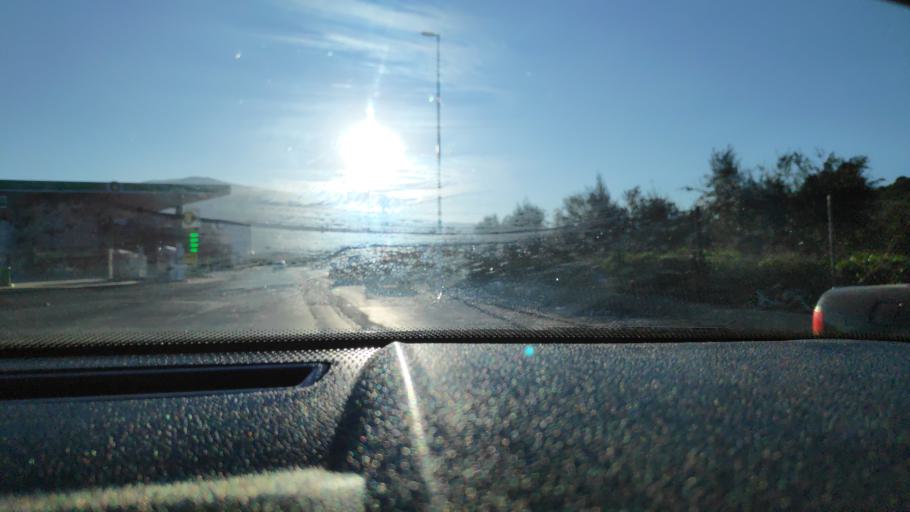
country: ES
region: Andalusia
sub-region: Provincia de Jaen
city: Jaen
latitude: 37.8003
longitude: -3.7905
